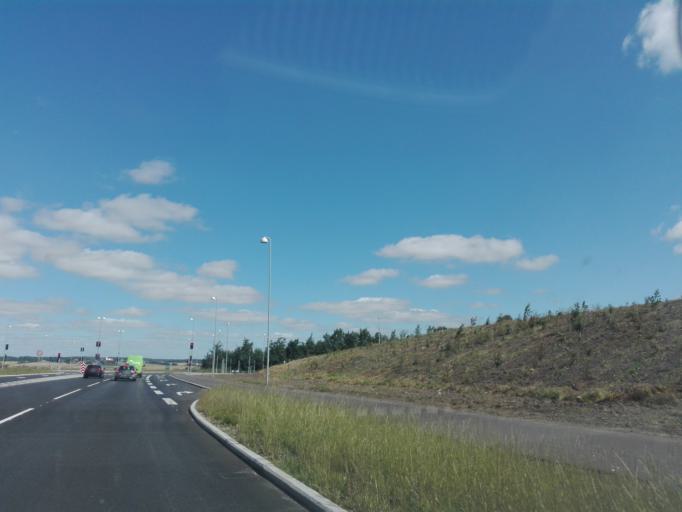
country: DK
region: Central Jutland
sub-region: Arhus Kommune
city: Trige
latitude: 56.1939
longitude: 10.1614
